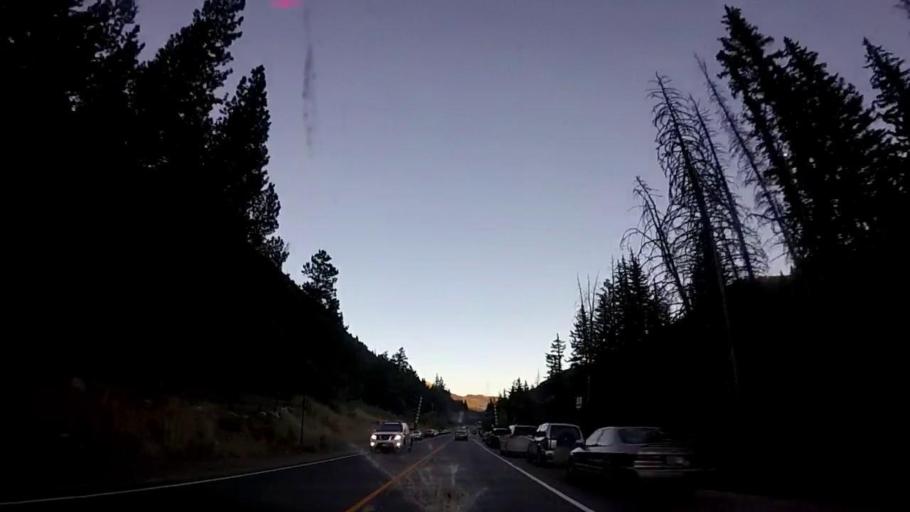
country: US
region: Utah
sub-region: Summit County
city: Summit Park
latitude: 40.6433
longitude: -111.6377
